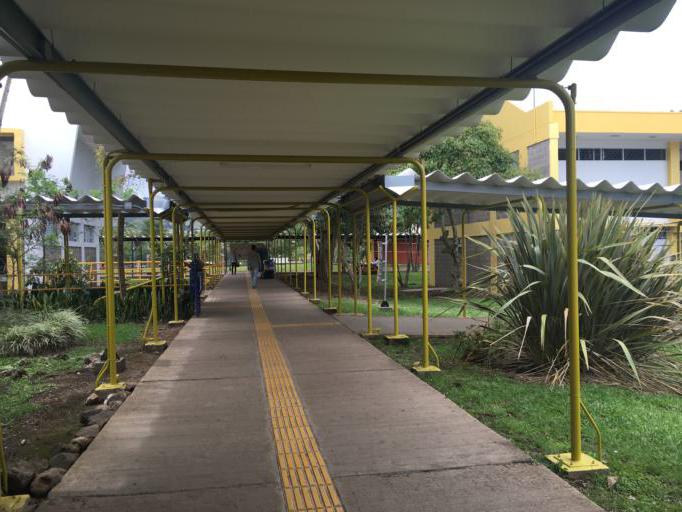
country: CR
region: Cartago
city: Cartago
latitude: 9.8550
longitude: -83.9093
